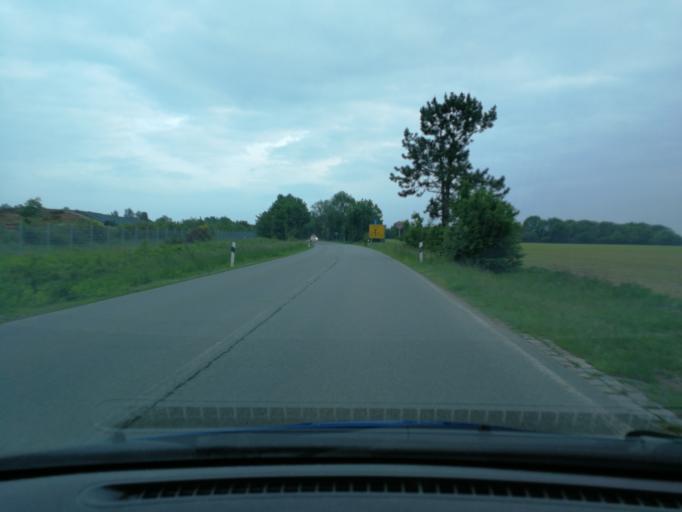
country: DE
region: Schleswig-Holstein
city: Siebeneichen
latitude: 53.5131
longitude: 10.6129
